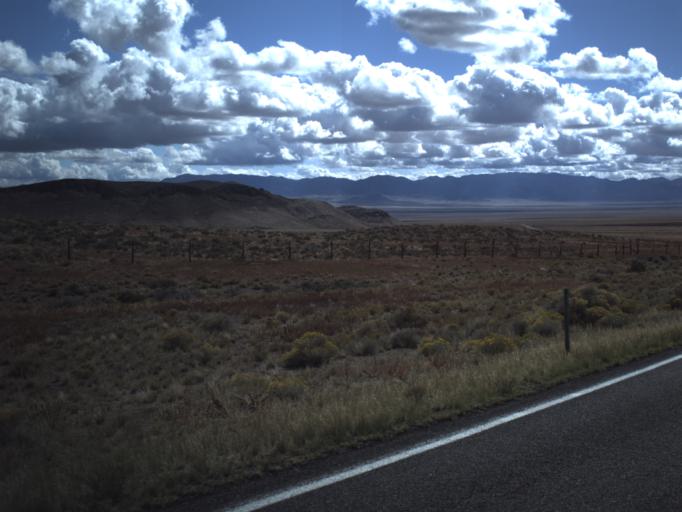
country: US
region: Utah
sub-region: Beaver County
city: Milford
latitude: 38.6048
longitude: -113.8346
